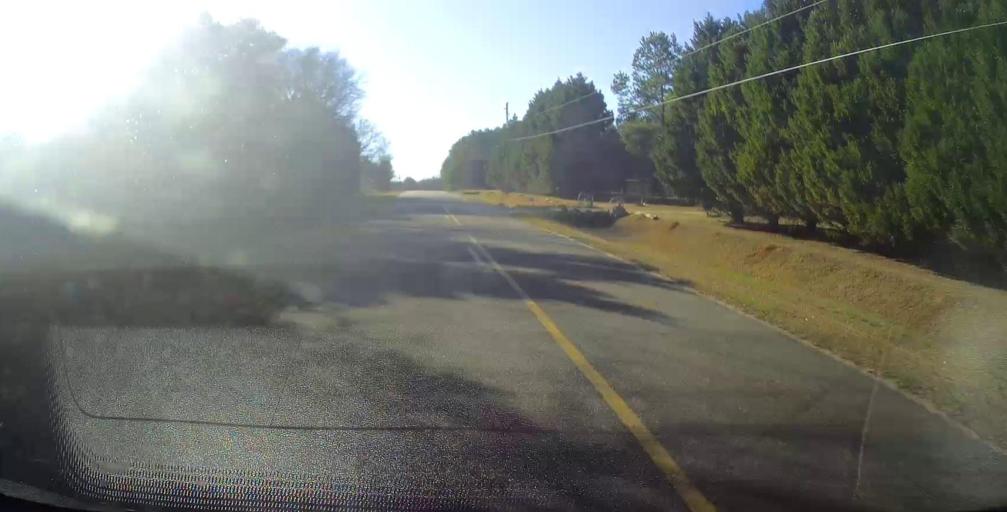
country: US
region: Georgia
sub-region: Sumter County
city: Americus
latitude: 32.0470
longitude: -84.2701
